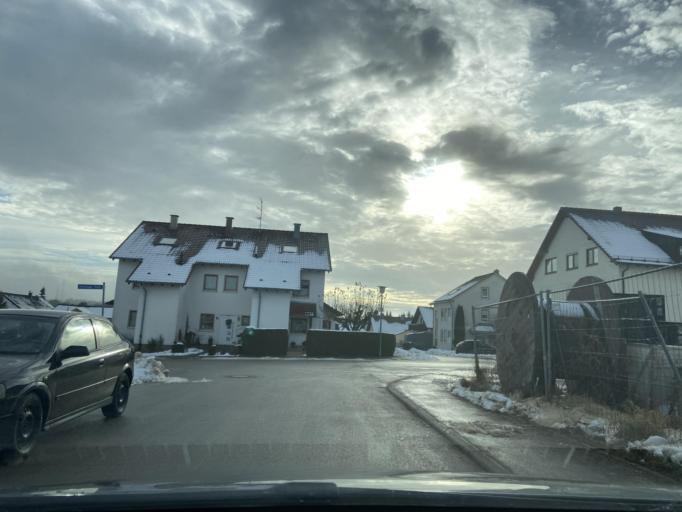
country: DE
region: Baden-Wuerttemberg
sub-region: Tuebingen Region
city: Neufra
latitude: 48.2431
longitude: 9.2035
